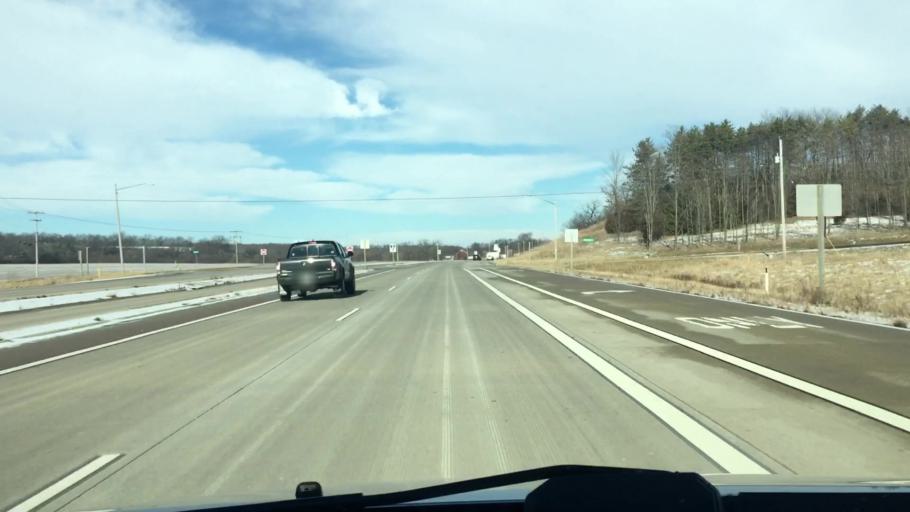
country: US
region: Wisconsin
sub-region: Waukesha County
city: Mukwonago
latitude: 42.8999
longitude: -88.3447
